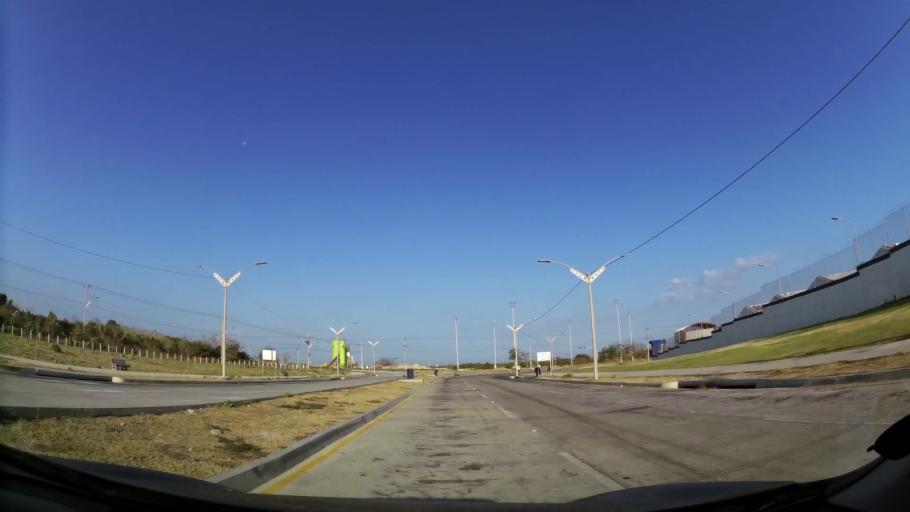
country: CO
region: Atlantico
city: Barranquilla
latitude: 11.0322
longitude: -74.8301
